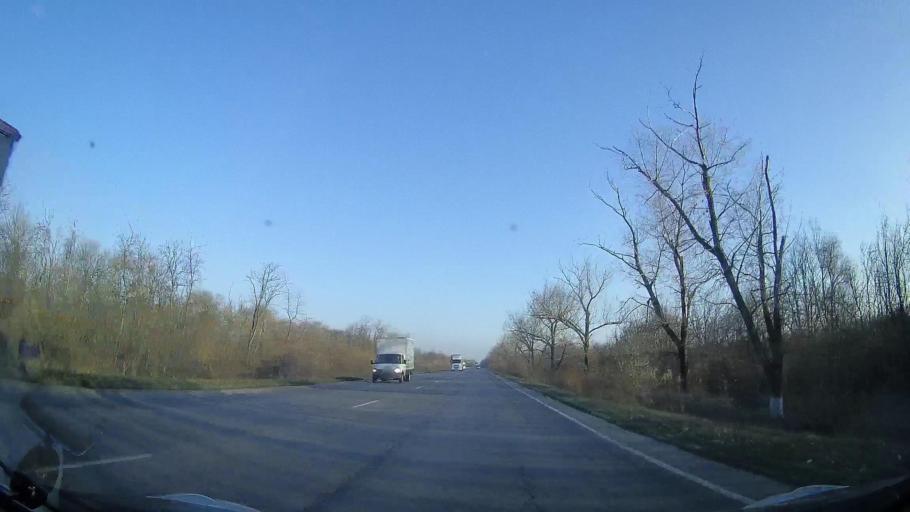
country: RU
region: Rostov
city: Bataysk
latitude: 47.0573
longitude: 39.8235
